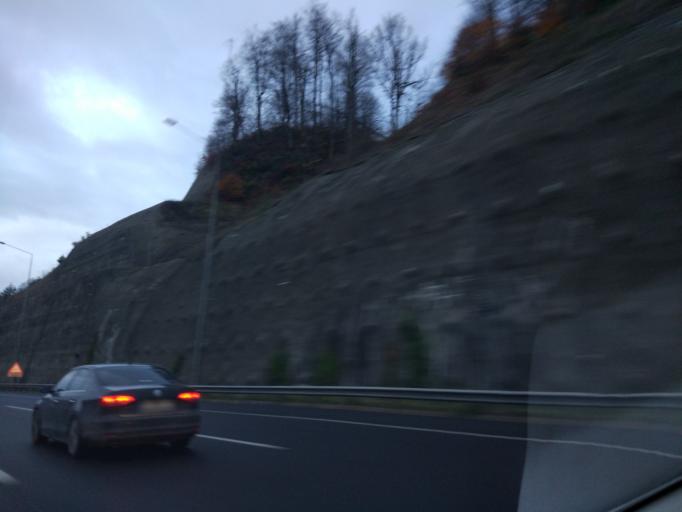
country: TR
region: Duzce
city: Kaynasli
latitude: 40.7587
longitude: 31.4460
